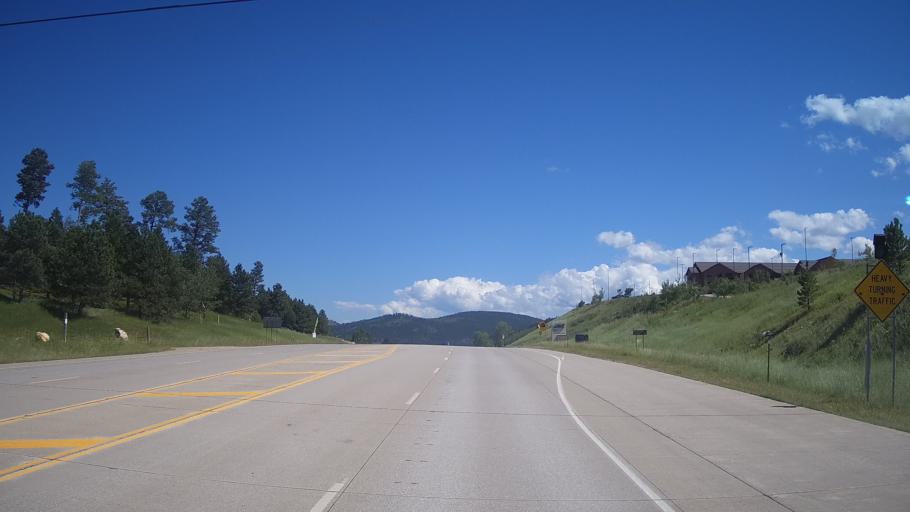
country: US
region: South Dakota
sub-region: Lawrence County
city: Deadwood
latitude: 44.3974
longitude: -103.7167
